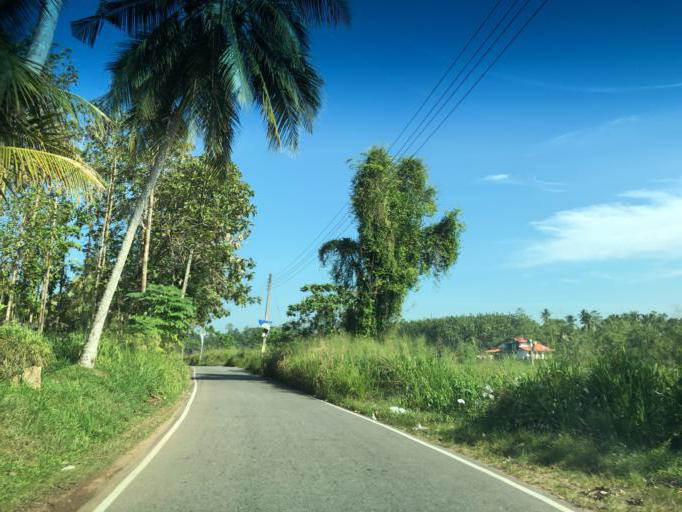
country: LK
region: Western
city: Homagama
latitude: 6.7991
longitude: 79.9819
